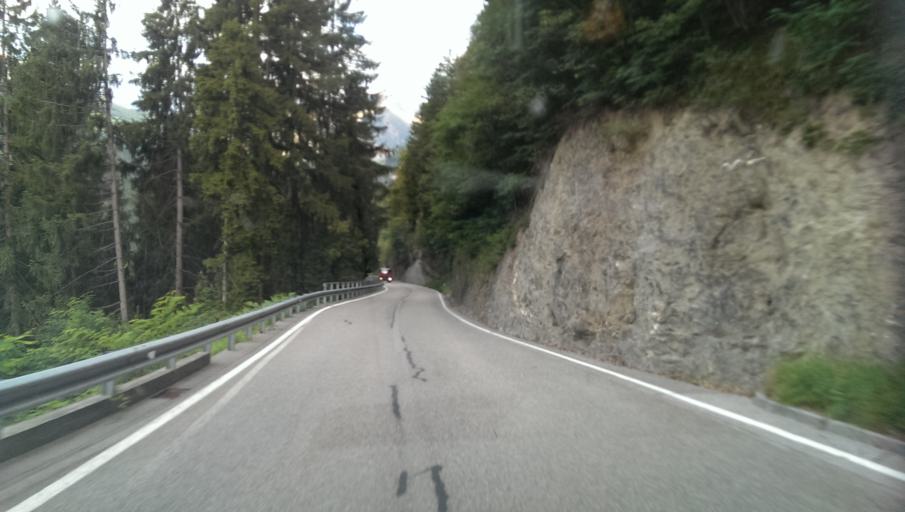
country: IT
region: Trentino-Alto Adige
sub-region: Bolzano
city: San Leonardo in Passiria
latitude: 46.8179
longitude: 11.2469
